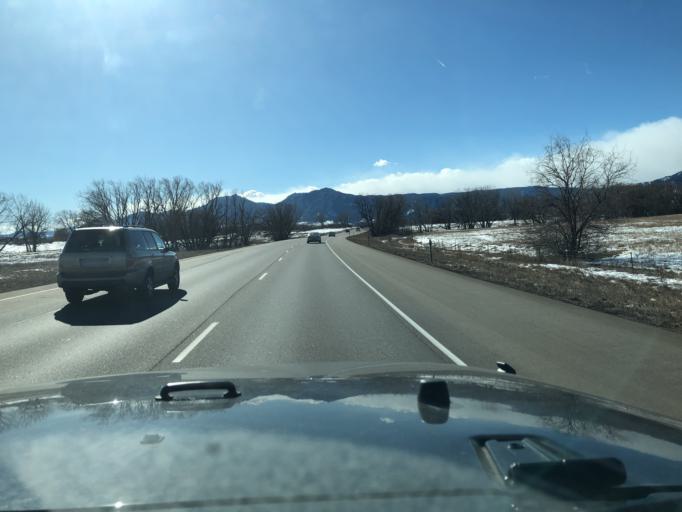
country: US
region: Colorado
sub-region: Boulder County
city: Gunbarrel
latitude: 40.0563
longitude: -105.2276
